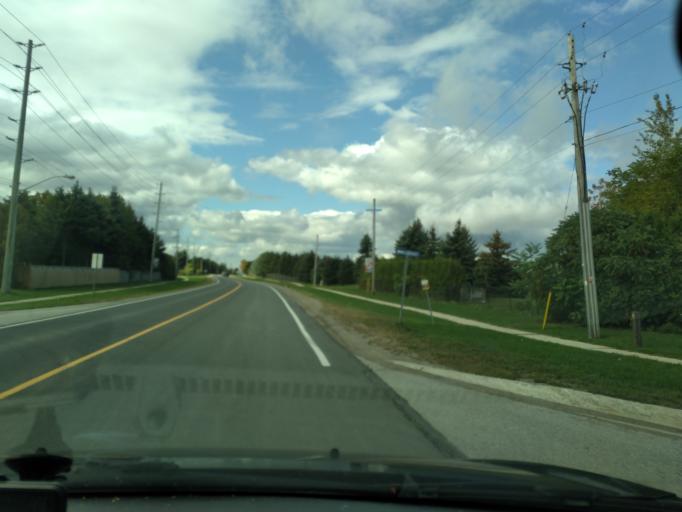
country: CA
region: Ontario
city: Innisfil
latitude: 44.2696
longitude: -79.7280
